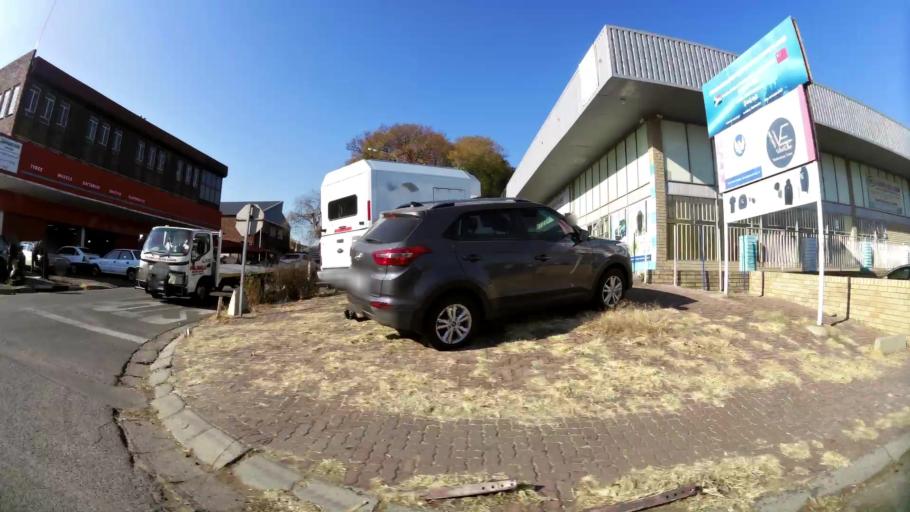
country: ZA
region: Gauteng
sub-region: City of Johannesburg Metropolitan Municipality
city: Modderfontein
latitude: -26.1327
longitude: 28.1472
